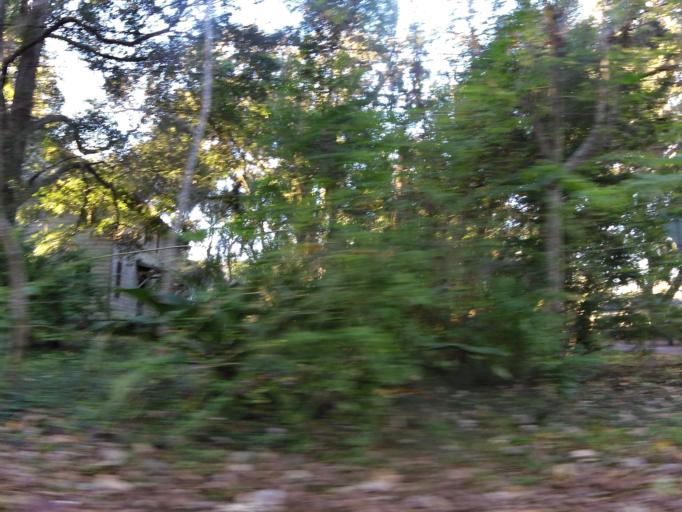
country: US
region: Florida
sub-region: Duval County
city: Jacksonville
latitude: 30.2720
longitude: -81.7055
